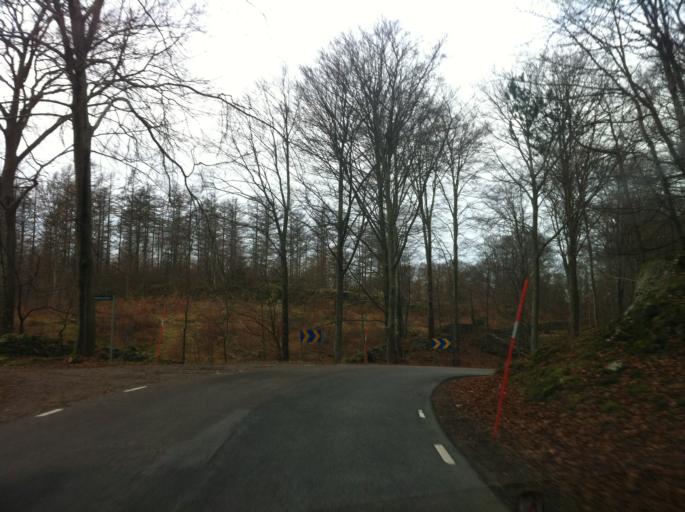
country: SE
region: Skane
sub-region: Svalovs Kommun
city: Kagerod
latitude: 56.0702
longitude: 13.1110
